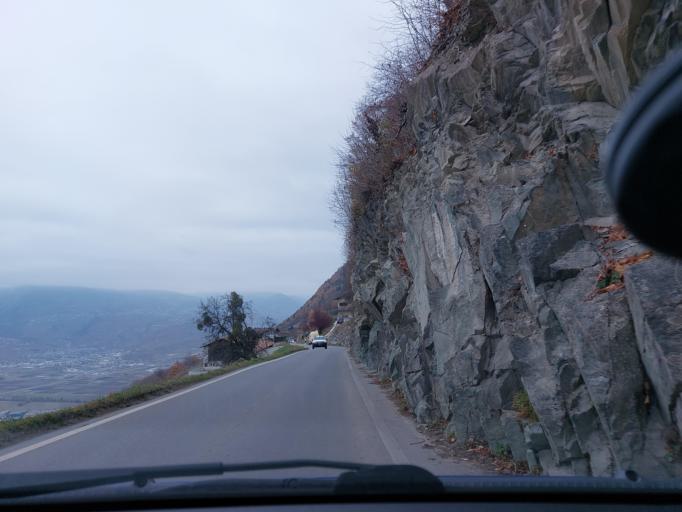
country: CH
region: Valais
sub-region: Conthey District
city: Ardon
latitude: 46.1800
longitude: 7.2649
